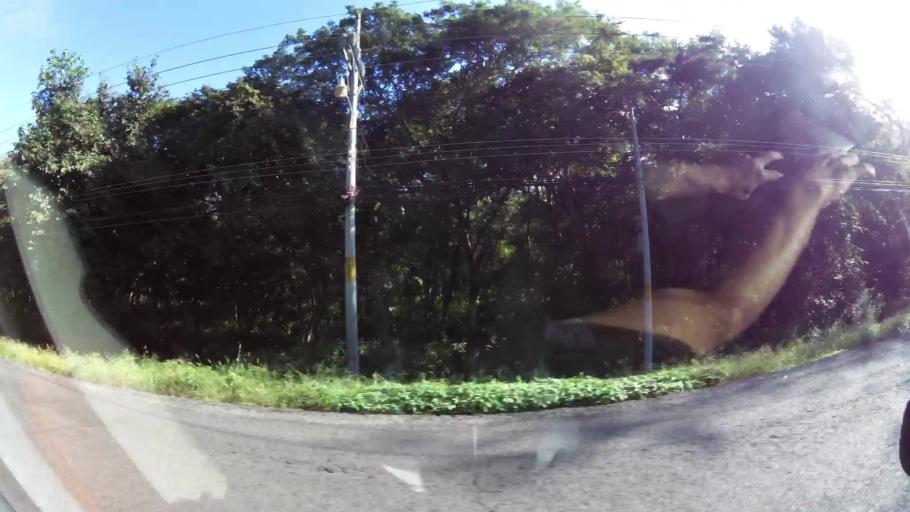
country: CR
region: Guanacaste
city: Sardinal
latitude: 10.5867
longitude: -85.6496
